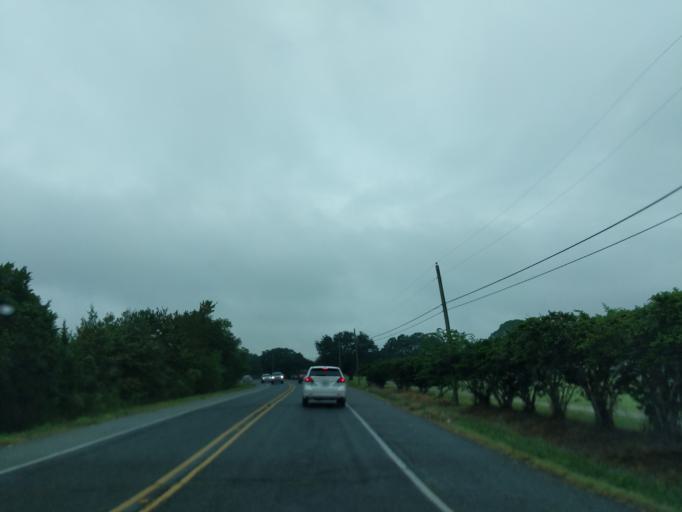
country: US
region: Louisiana
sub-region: Vermilion Parish
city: Abbeville
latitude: 29.9867
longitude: -92.1592
